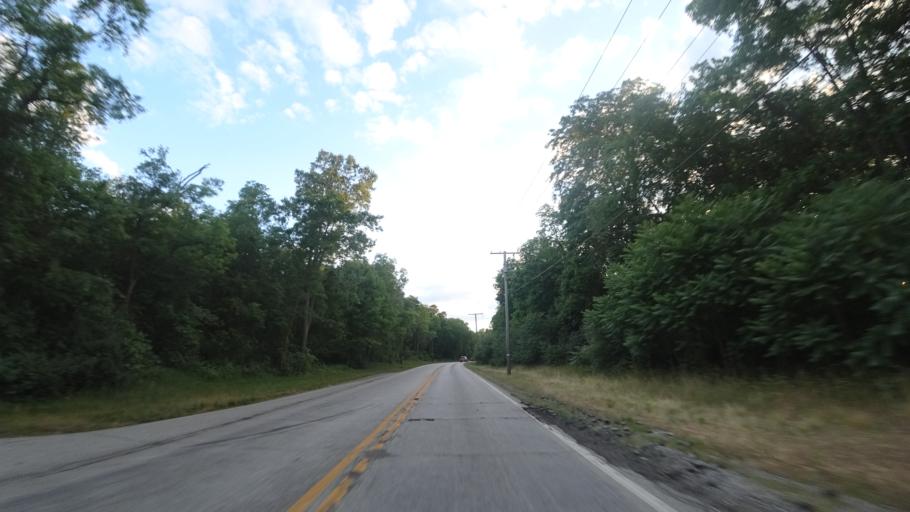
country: US
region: Indiana
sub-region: Porter County
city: Porter
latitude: 41.6380
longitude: -87.0770
